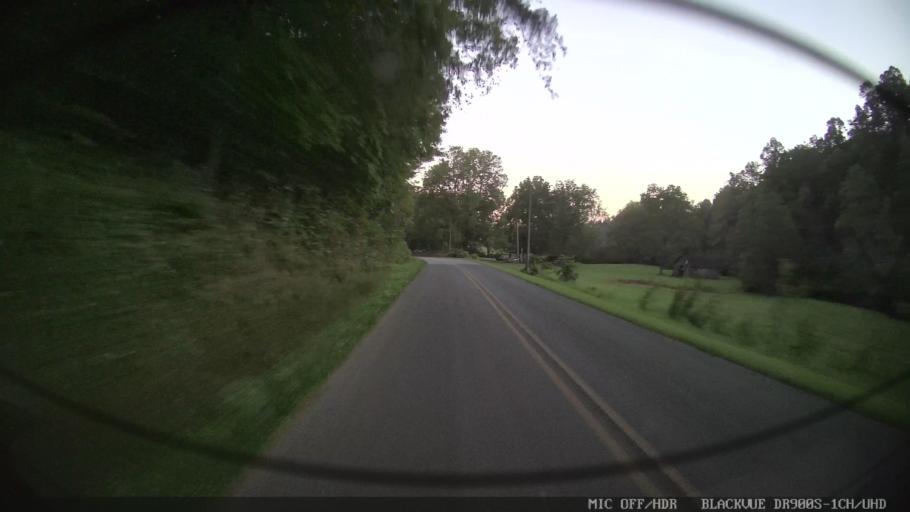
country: US
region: Georgia
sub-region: Gilmer County
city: Ellijay
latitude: 34.7747
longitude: -84.5380
